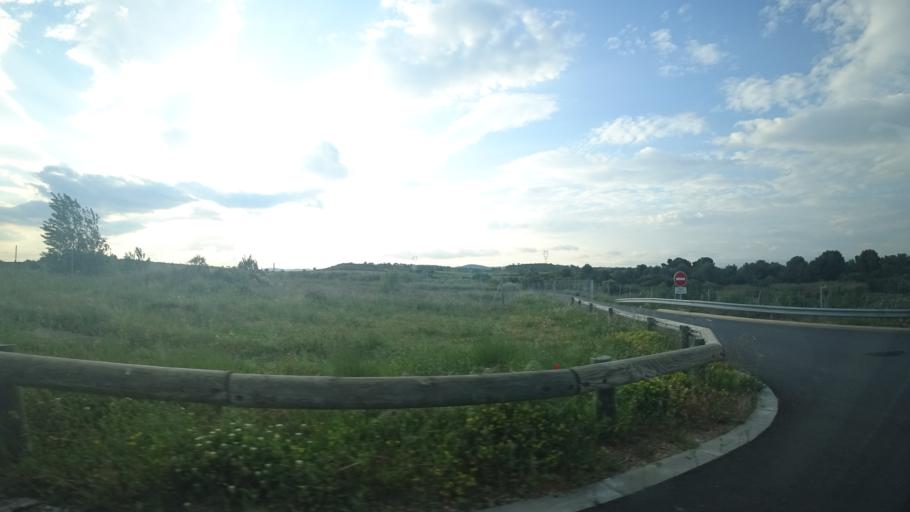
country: FR
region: Languedoc-Roussillon
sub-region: Departement de l'Herault
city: Paulhan
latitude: 43.5446
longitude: 3.4460
